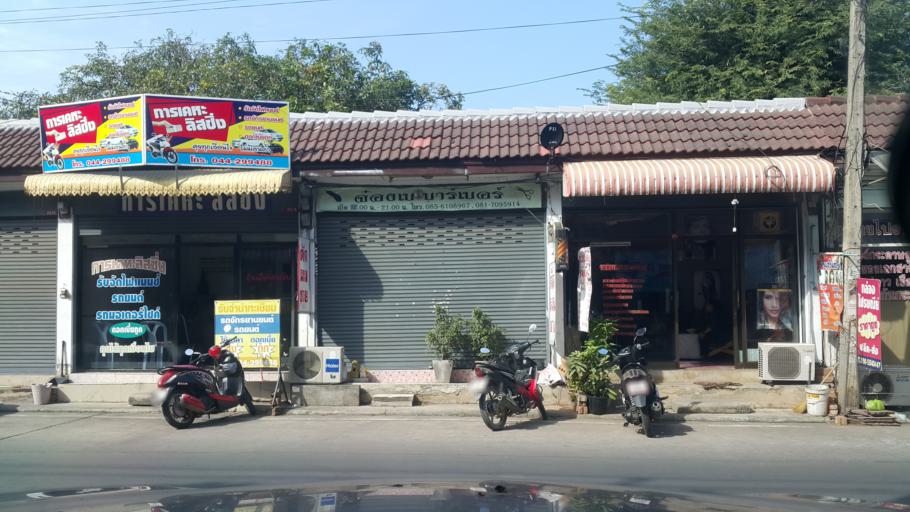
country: TH
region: Nakhon Ratchasima
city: Nakhon Ratchasima
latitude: 14.9523
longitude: 102.0444
